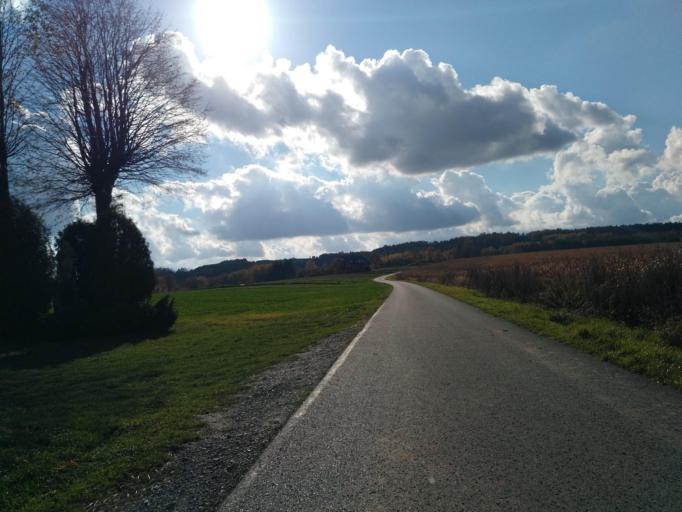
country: PL
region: Subcarpathian Voivodeship
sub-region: Powiat rzeszowski
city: Zglobien
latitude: 49.9919
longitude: 21.8495
